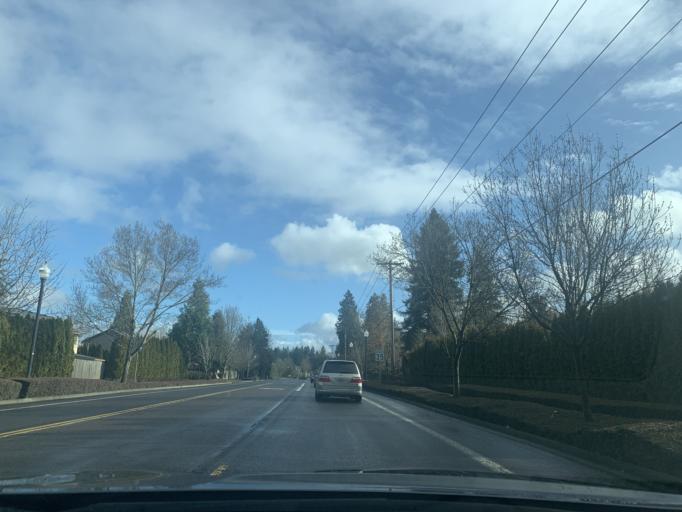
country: US
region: Oregon
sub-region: Washington County
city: Sherwood
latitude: 45.3714
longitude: -122.8541
